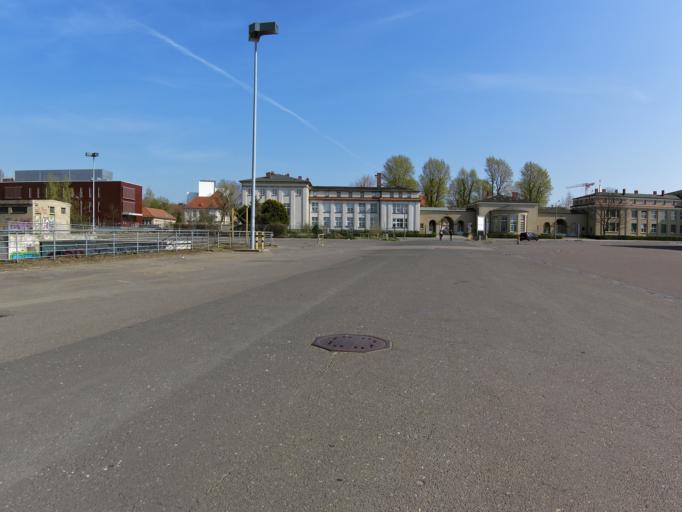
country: DE
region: Saxony
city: Leipzig
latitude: 51.3194
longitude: 12.3897
